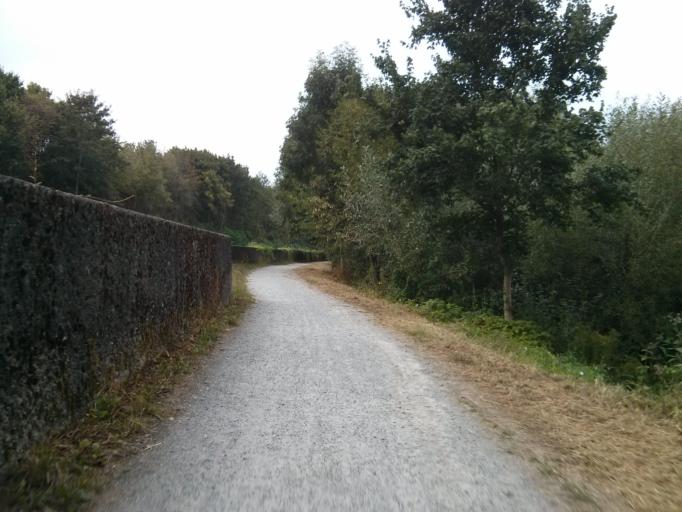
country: DE
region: Bavaria
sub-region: Lower Bavaria
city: Deggendorf
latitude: 48.8453
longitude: 12.9553
